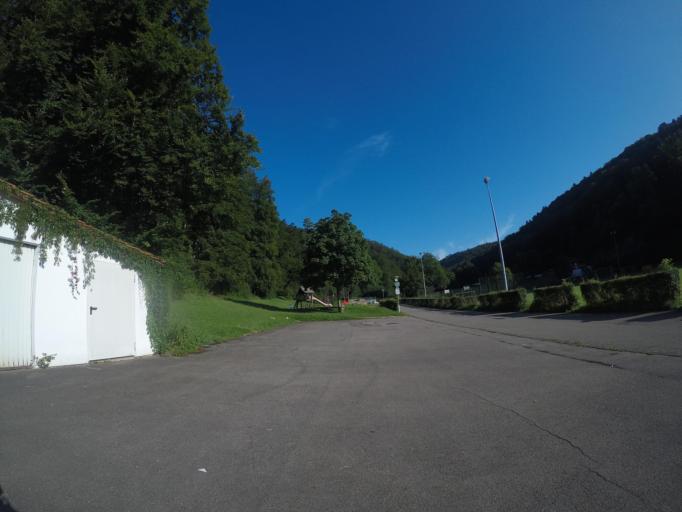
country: DE
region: Baden-Wuerttemberg
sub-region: Tuebingen Region
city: Schelklingen
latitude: 48.3783
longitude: 9.7339
